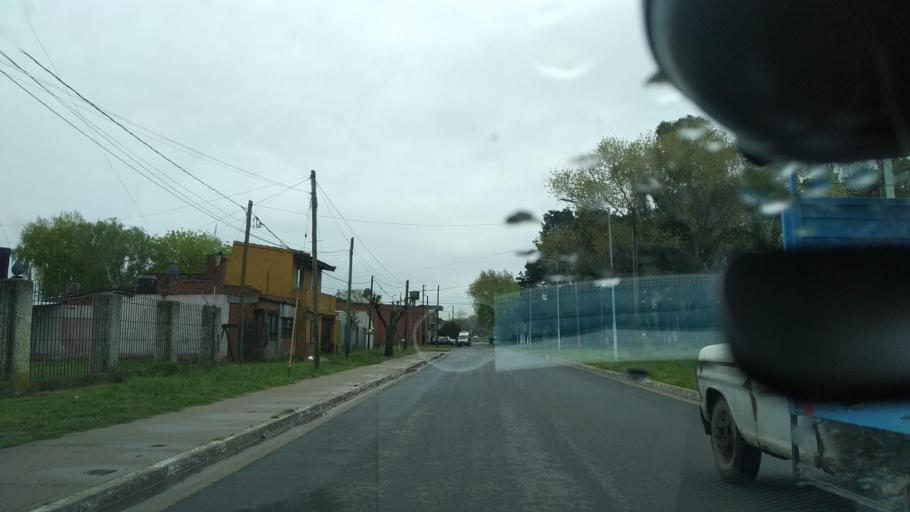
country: AR
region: Buenos Aires
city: Mar del Tuyu
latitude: -36.5360
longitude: -56.7128
